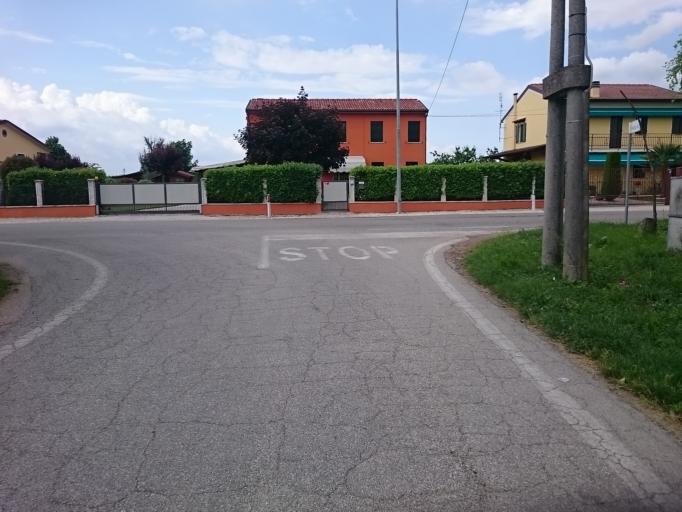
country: IT
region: Veneto
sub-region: Provincia di Padova
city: Ponso
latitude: 45.1998
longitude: 11.5739
